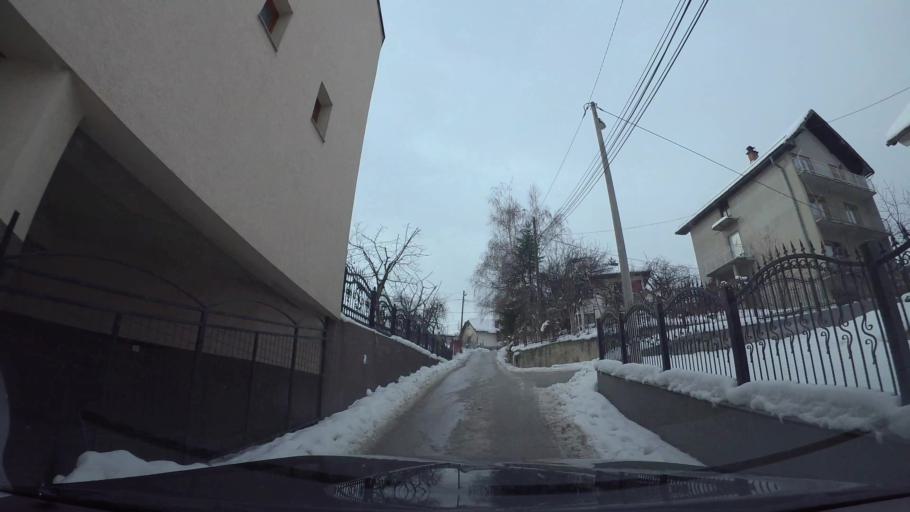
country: BA
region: Federation of Bosnia and Herzegovina
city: Kobilja Glava
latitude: 43.8703
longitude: 18.3972
